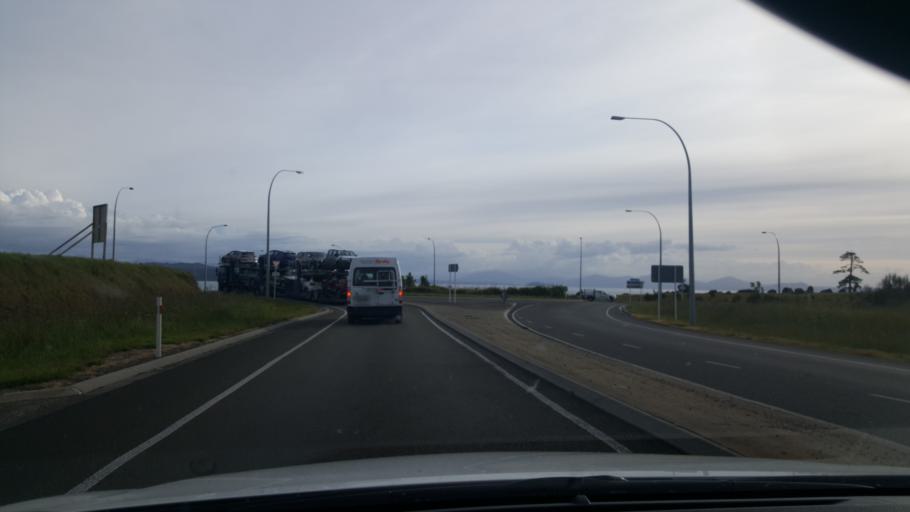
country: NZ
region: Waikato
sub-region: Taupo District
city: Taupo
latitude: -38.7381
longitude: 176.0733
